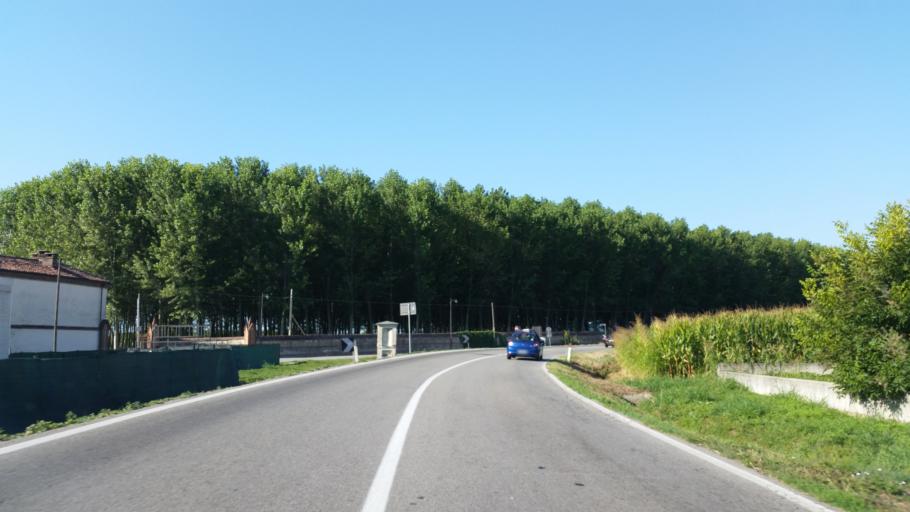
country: IT
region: Piedmont
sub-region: Provincia di Cuneo
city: Cinzano
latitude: 44.6808
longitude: 7.8910
